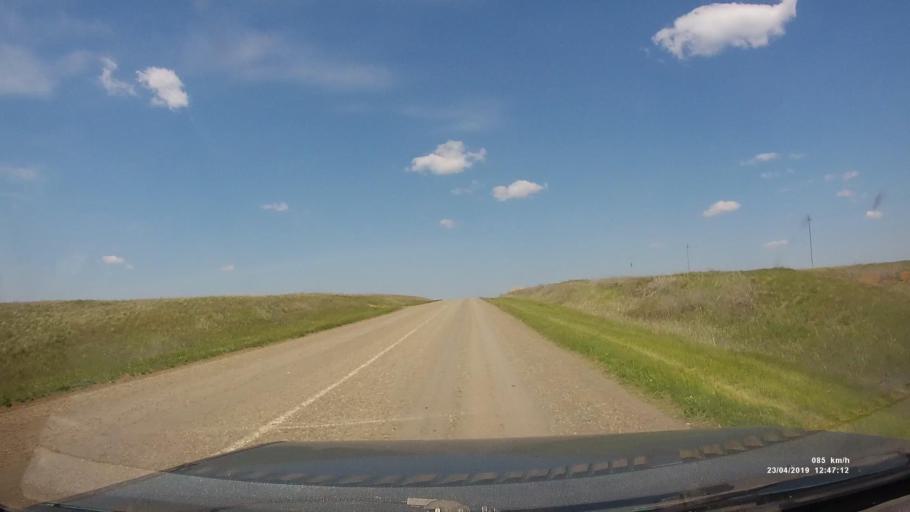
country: RU
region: Kalmykiya
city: Yashalta
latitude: 46.5091
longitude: 42.6386
